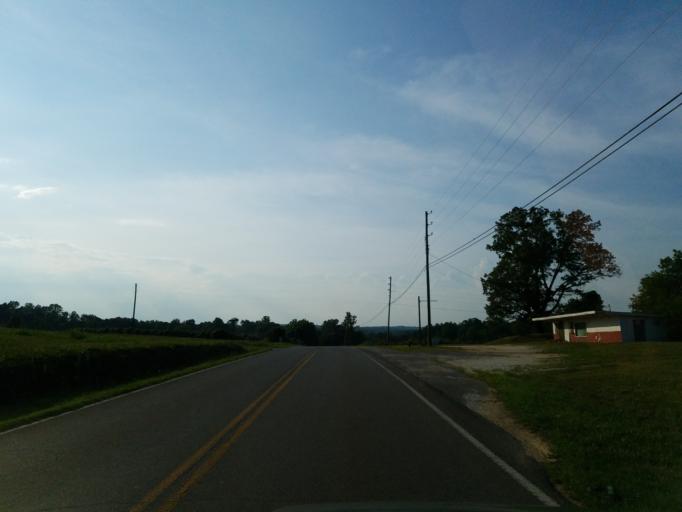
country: US
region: Georgia
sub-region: Pickens County
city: Jasper
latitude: 34.5370
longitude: -84.5335
